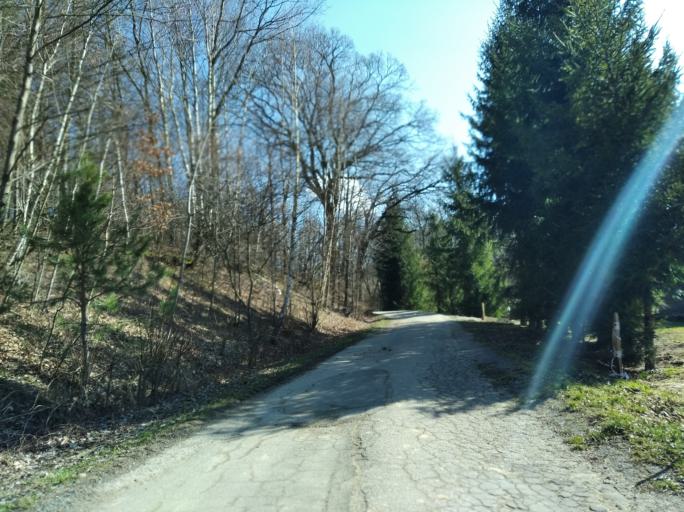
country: PL
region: Subcarpathian Voivodeship
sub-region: Powiat strzyzowski
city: Wysoka Strzyzowska
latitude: 49.8088
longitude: 21.7501
